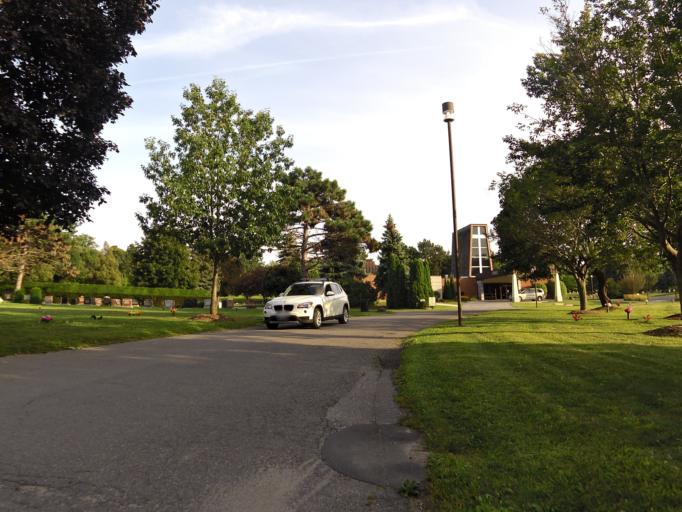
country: CA
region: Ontario
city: Bells Corners
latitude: 45.3413
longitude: -75.7846
